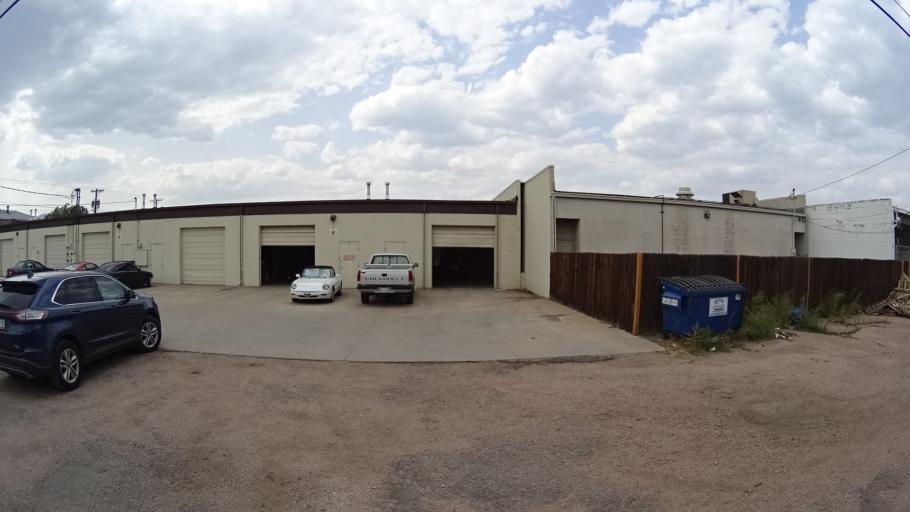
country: US
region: Colorado
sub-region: El Paso County
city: Colorado Springs
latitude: 38.8367
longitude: -104.7739
